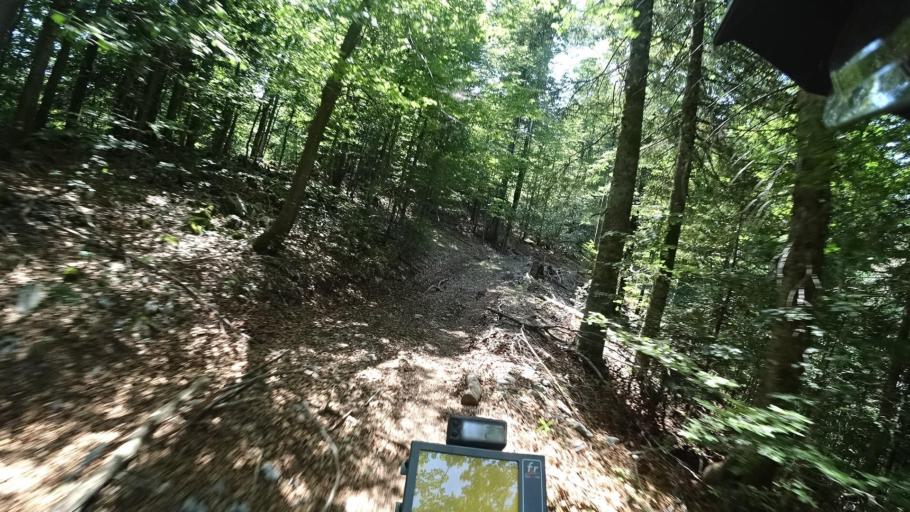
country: HR
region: Primorsko-Goranska
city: Bribir
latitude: 45.2700
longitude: 14.8421
